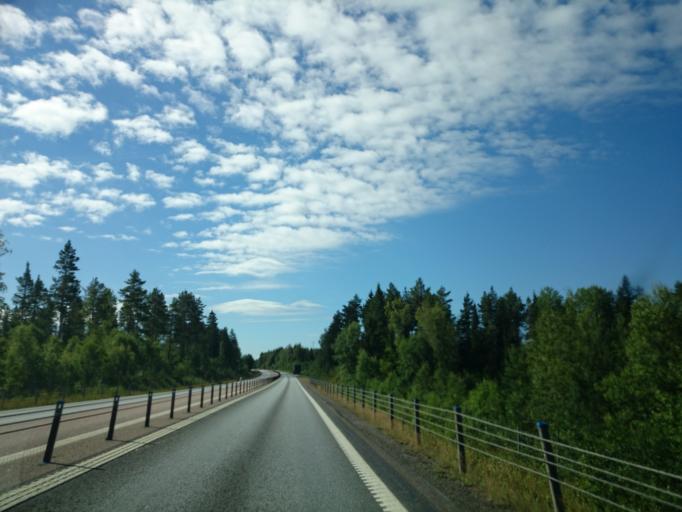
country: SE
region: Gaevleborg
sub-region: Soderhamns Kommun
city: Soderhamn
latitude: 61.2506
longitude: 17.0337
